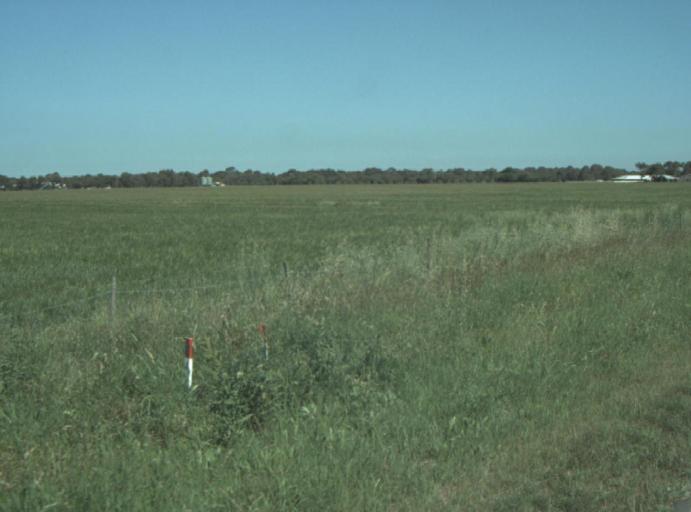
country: AU
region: Victoria
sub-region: Greater Geelong
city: Lara
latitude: -37.9897
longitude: 144.4023
